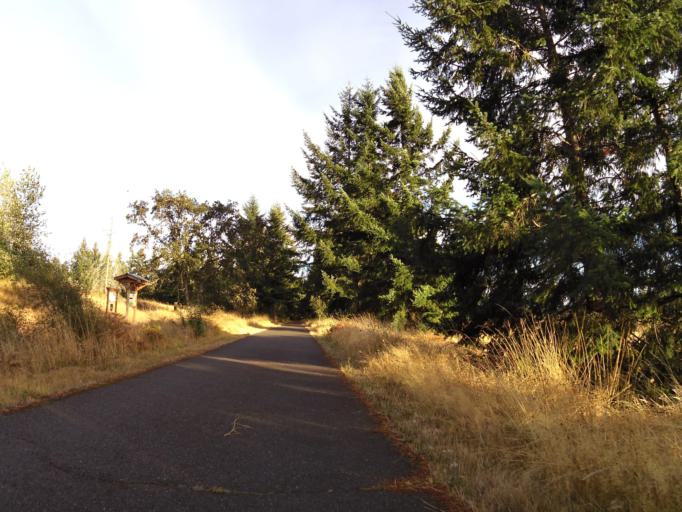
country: US
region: Washington
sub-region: Thurston County
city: Rainier
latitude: 46.8777
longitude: -122.7315
